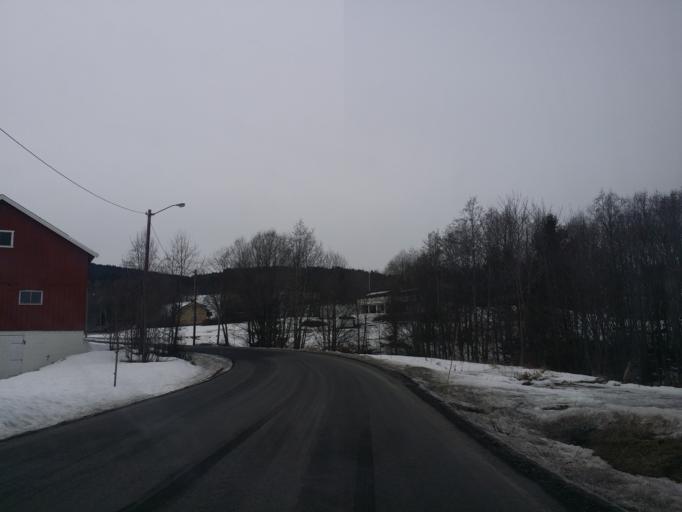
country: NO
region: Buskerud
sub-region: Lier
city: Tranby
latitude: 59.8529
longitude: 10.2212
